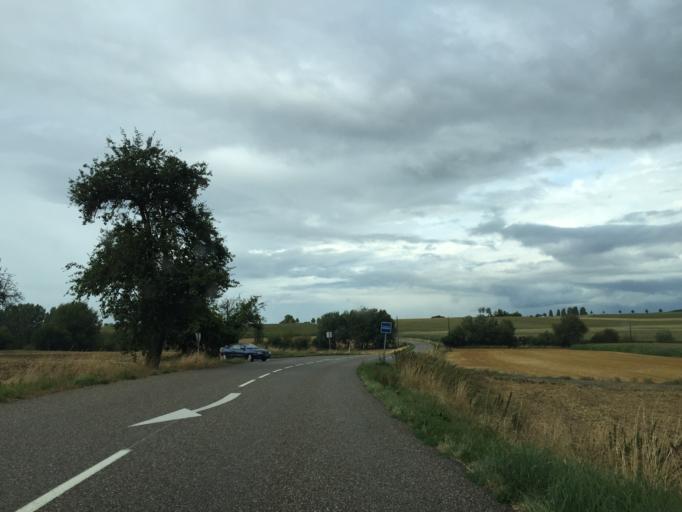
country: FR
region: Alsace
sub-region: Departement du Bas-Rhin
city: Soultz-sous-Forets
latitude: 48.9611
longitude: 7.9241
